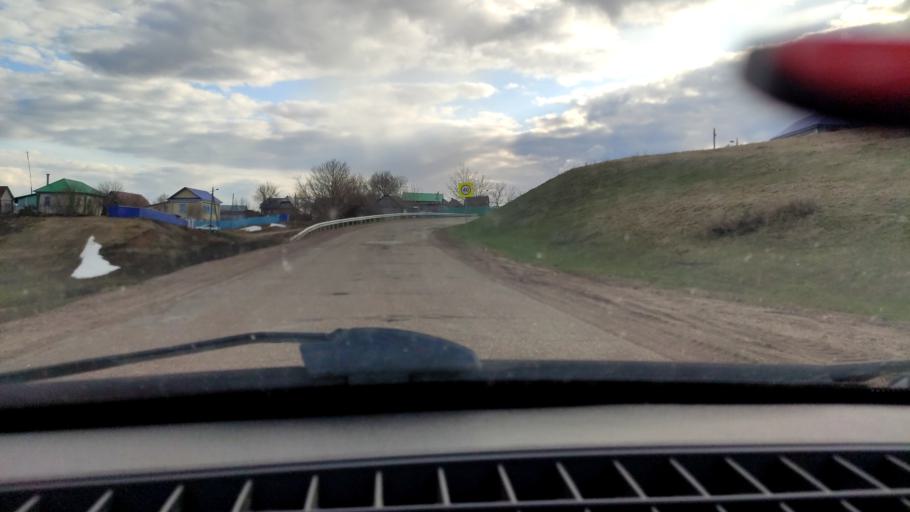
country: RU
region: Bashkortostan
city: Karmaskaly
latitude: 54.3366
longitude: 56.0057
